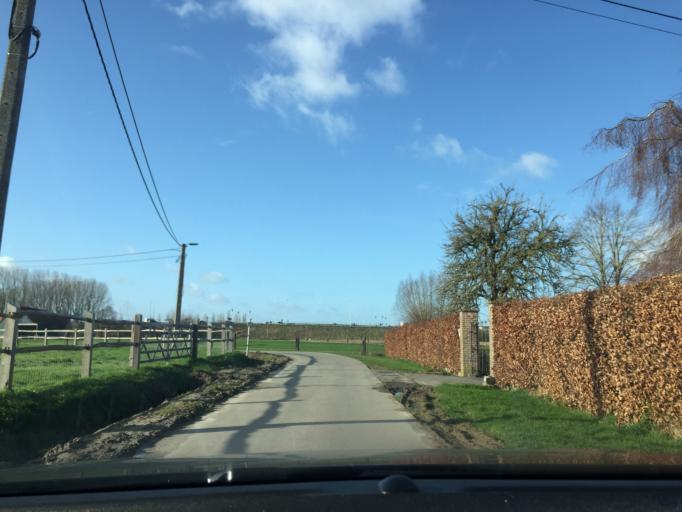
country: BE
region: Flanders
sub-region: Provincie West-Vlaanderen
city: Ardooie
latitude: 50.9732
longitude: 3.1826
